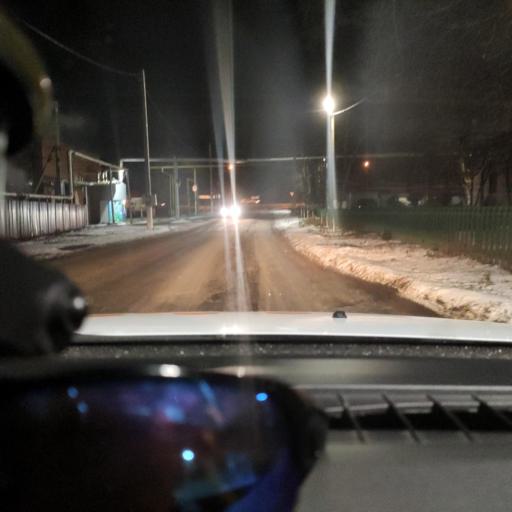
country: RU
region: Samara
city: Samara
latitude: 53.0820
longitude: 50.0920
